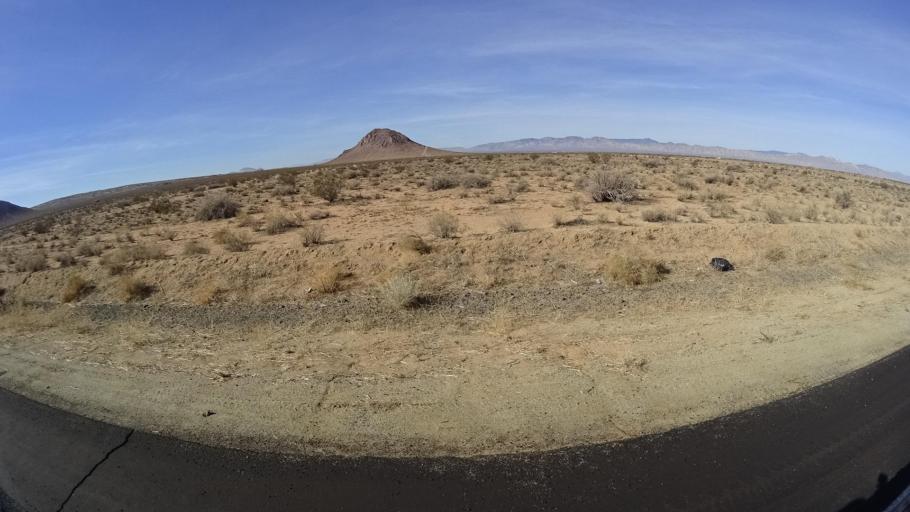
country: US
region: California
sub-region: Kern County
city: California City
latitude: 35.0883
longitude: -117.9175
